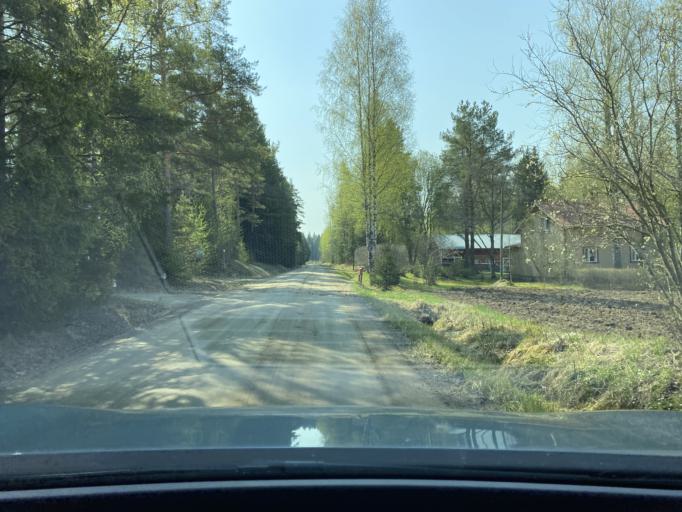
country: FI
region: Satakunta
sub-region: Pori
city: Huittinen
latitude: 61.1336
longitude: 22.8352
